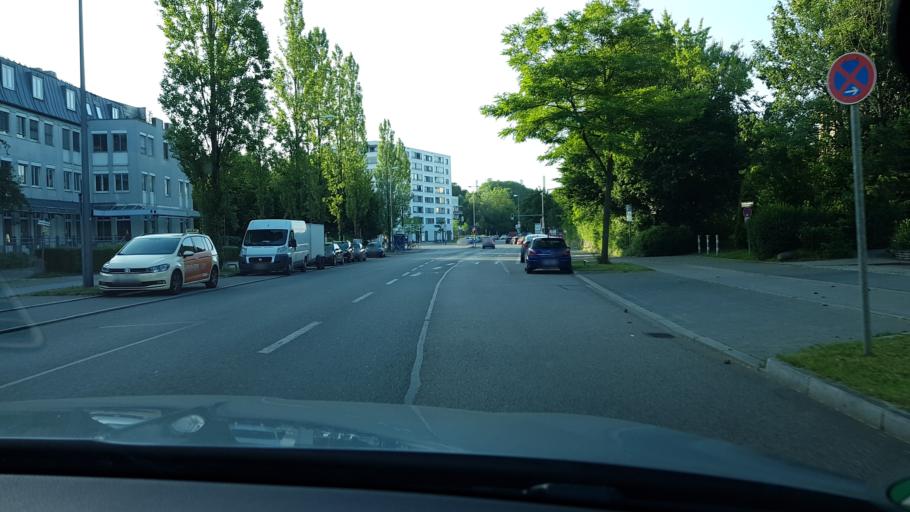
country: DE
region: Bavaria
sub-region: Upper Bavaria
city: Unterfoehring
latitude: 48.1664
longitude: 11.6441
